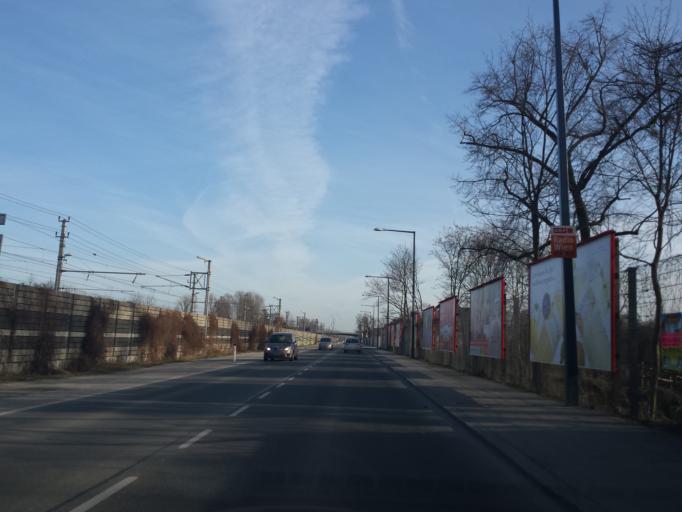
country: AT
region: Lower Austria
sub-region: Politischer Bezirk Wien-Umgebung
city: Schwechat
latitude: 48.1970
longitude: 16.4453
